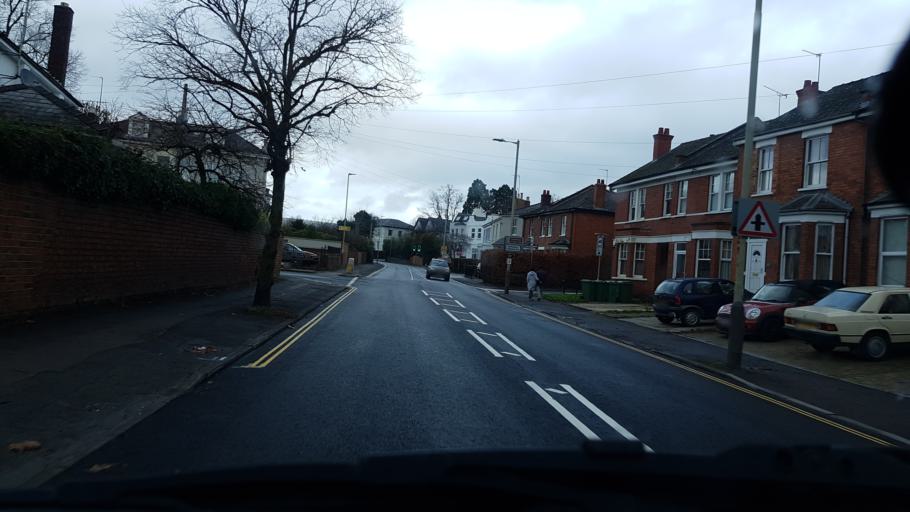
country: GB
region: England
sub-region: Gloucestershire
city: Cheltenham
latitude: 51.8954
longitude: -2.0616
